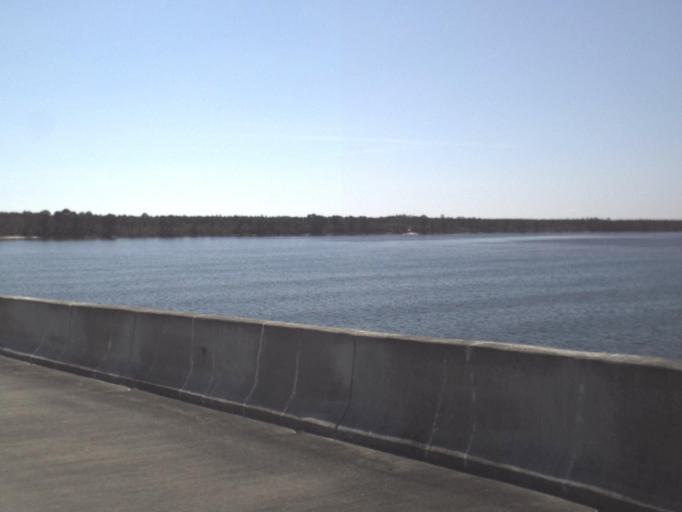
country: US
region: Florida
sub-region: Wakulla County
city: Crawfordville
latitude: 29.9672
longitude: -84.3841
